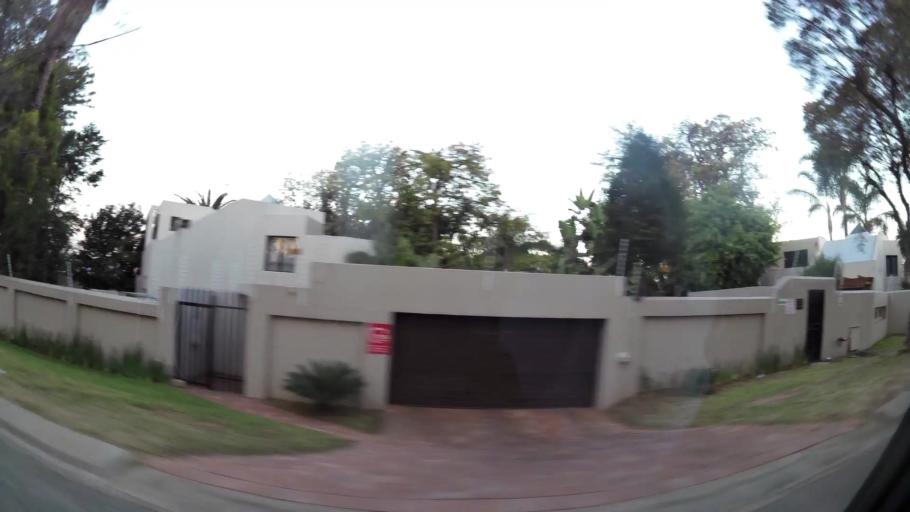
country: ZA
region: Gauteng
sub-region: City of Johannesburg Metropolitan Municipality
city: Diepsloot
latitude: -26.0305
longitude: 28.0236
